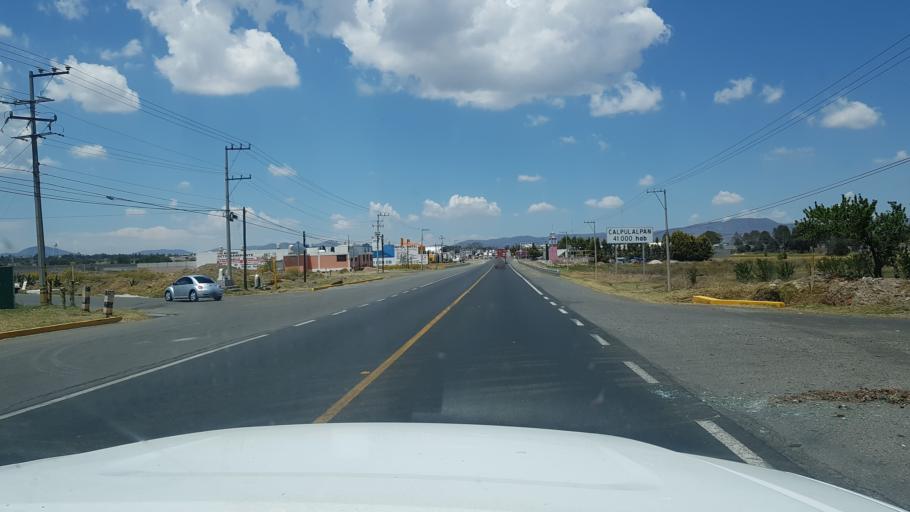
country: MX
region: Hidalgo
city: Calpulalpan
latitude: 19.5840
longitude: -98.5387
